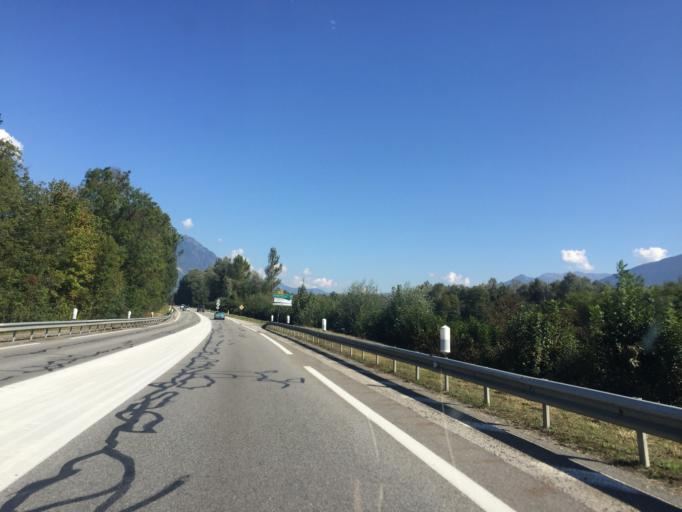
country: FR
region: Rhone-Alpes
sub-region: Departement de la Savoie
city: Gresy-sur-Isere
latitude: 45.5849
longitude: 6.2701
